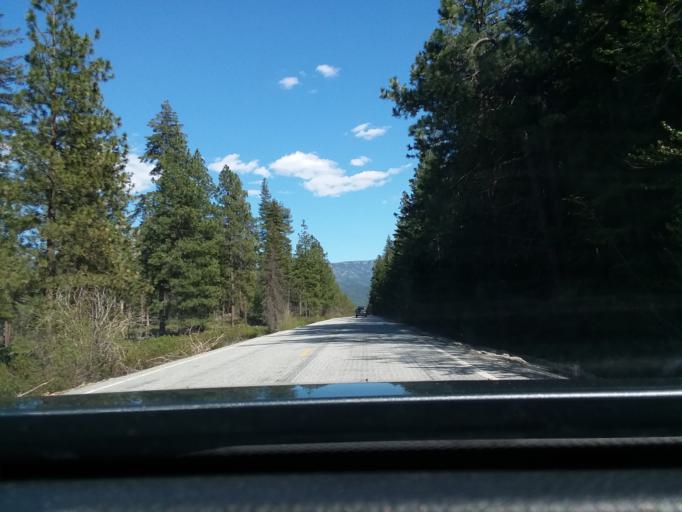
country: US
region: Washington
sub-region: Chelan County
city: Leavenworth
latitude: 47.8031
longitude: -120.6916
